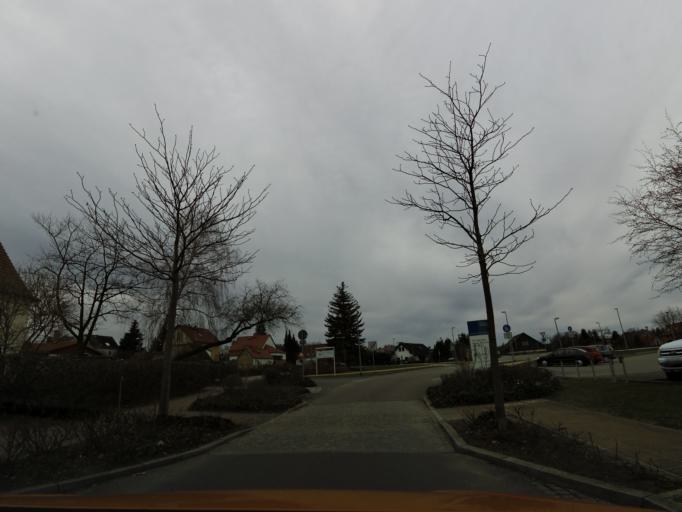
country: DE
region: Brandenburg
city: Belzig
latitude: 52.1421
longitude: 12.6004
